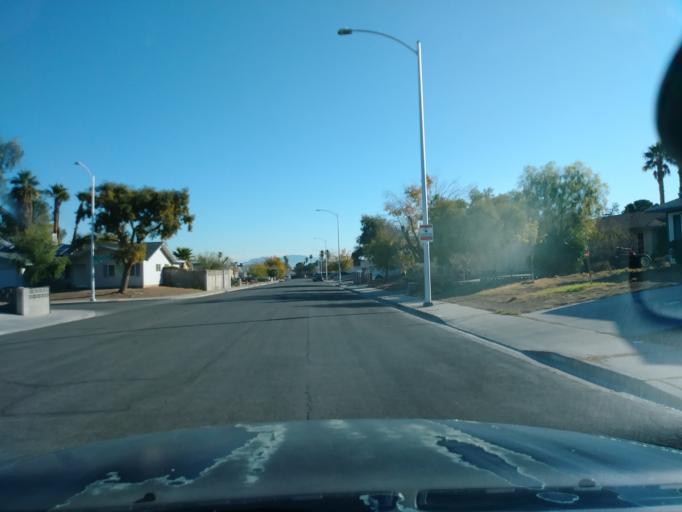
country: US
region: Nevada
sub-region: Clark County
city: Spring Valley
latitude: 36.1702
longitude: -115.2503
